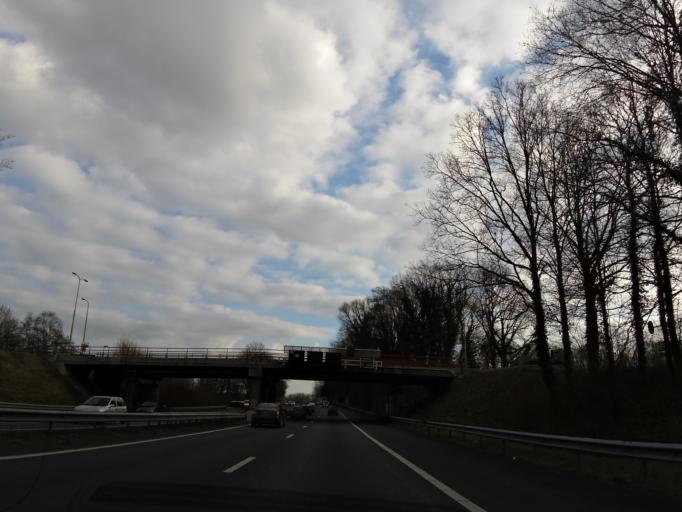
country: NL
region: Limburg
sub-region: Gemeente Nuth
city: Nuth
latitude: 50.9238
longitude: 5.8882
